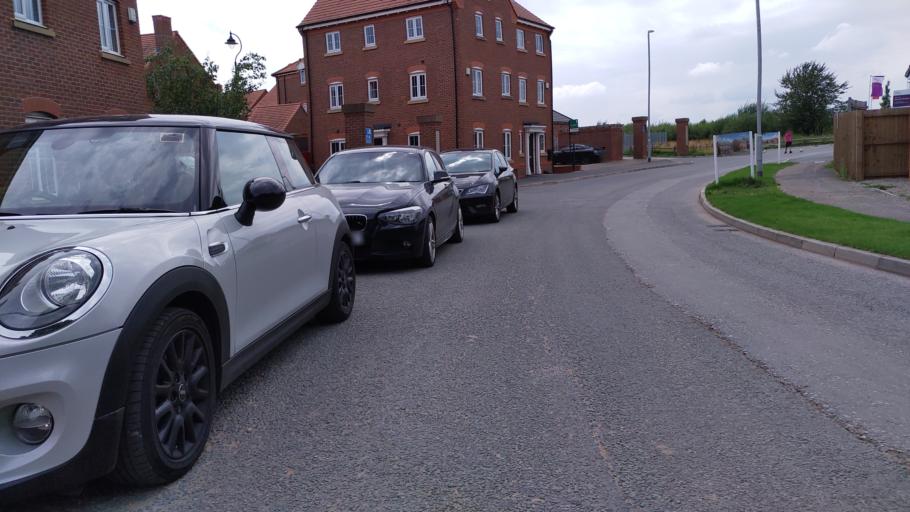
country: GB
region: England
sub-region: Lancashire
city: Coppull
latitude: 53.6308
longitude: -2.6389
